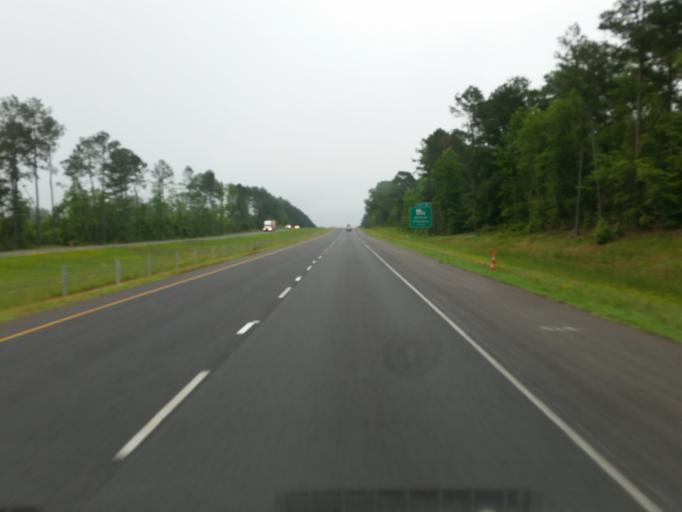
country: US
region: Louisiana
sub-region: Bienville Parish
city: Arcadia
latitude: 32.5633
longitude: -93.0772
